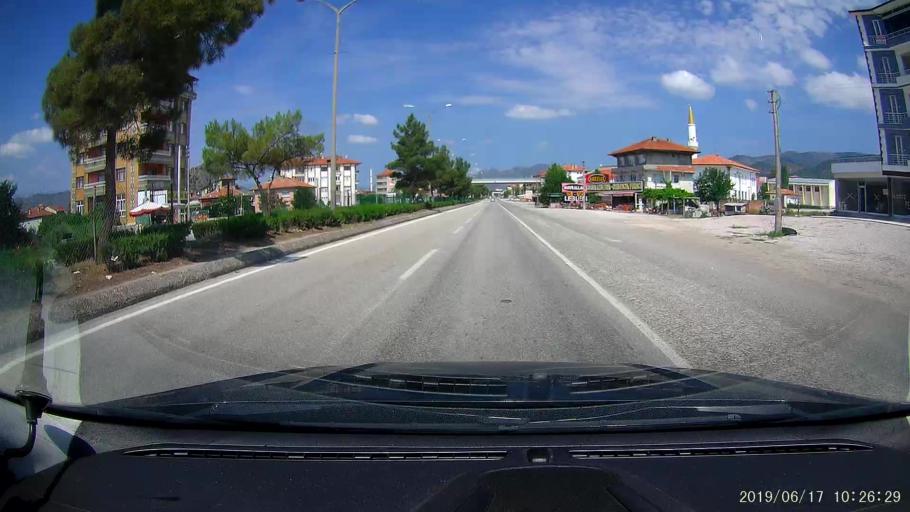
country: TR
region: Corum
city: Osmancik
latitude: 40.9737
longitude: 34.8184
